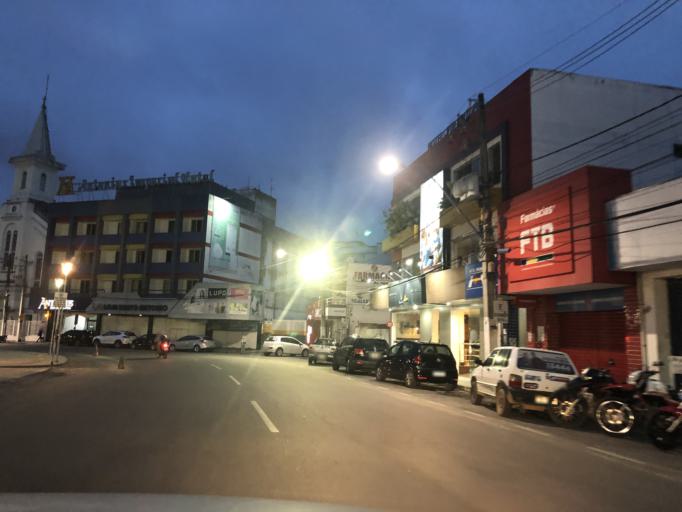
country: BR
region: Bahia
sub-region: Santo Antonio De Jesus
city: Santo Antonio de Jesus
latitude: -12.9691
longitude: -39.2636
